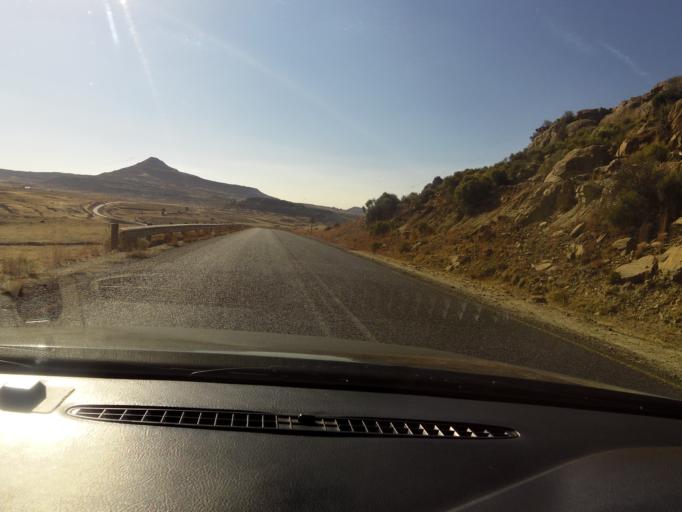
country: LS
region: Mohale's Hoek District
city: Mohale's Hoek
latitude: -30.0942
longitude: 27.4387
